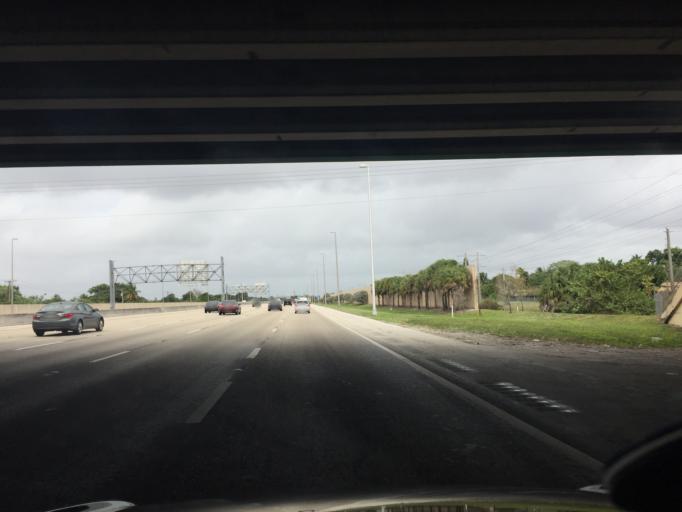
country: US
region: Florida
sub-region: Broward County
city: Broadview Park
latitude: 26.1045
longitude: -80.2194
